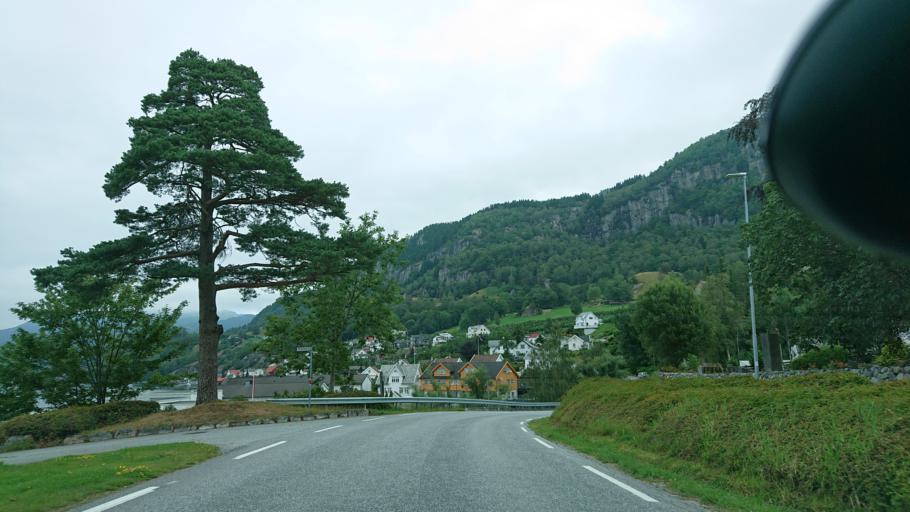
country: NO
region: Rogaland
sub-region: Hjelmeland
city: Hjelmelandsvagen
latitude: 59.2355
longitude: 6.1794
